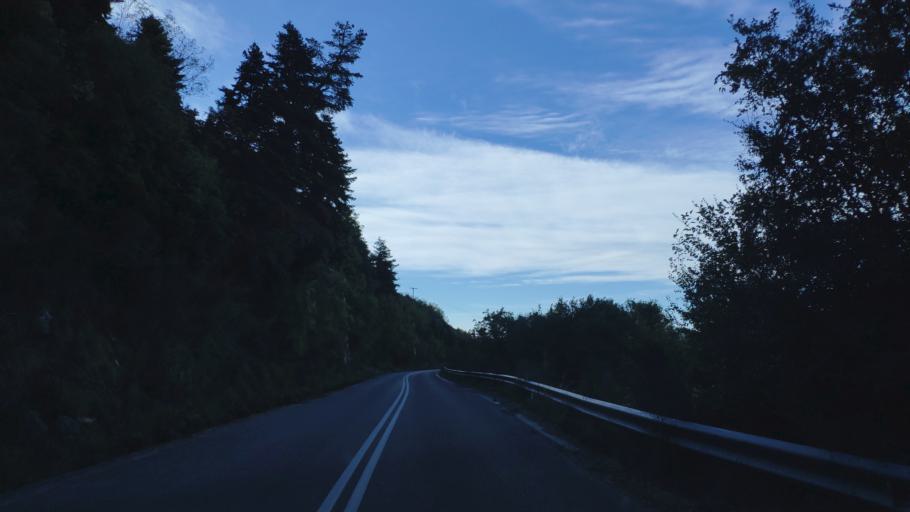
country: GR
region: Peloponnese
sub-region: Nomos Arkadias
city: Dimitsana
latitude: 37.5741
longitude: 22.0620
